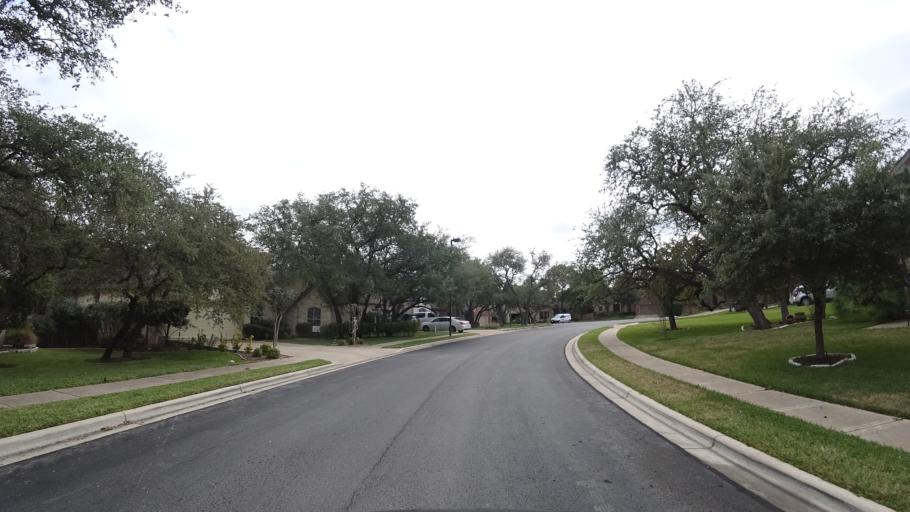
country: US
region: Texas
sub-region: Travis County
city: Shady Hollow
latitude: 30.1892
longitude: -97.9021
